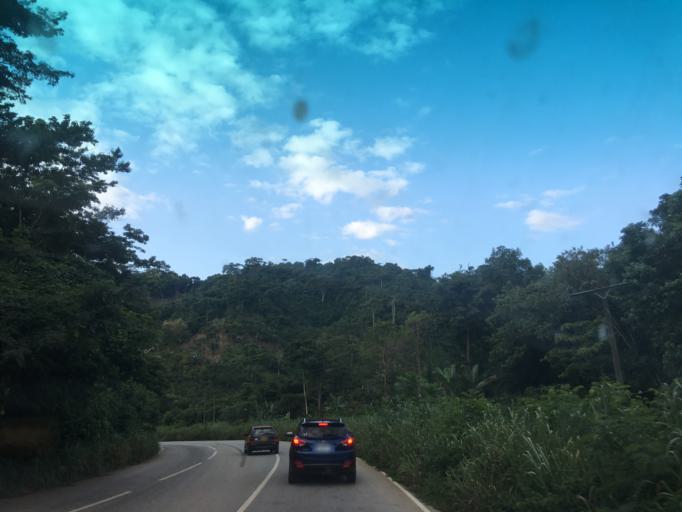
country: GH
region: Western
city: Bibiani
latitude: 6.4789
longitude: -2.3316
